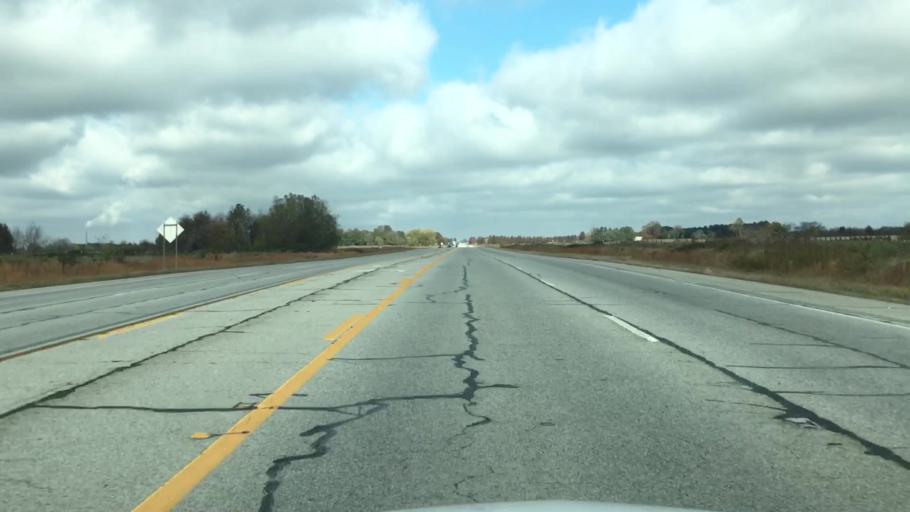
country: US
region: Arkansas
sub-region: Benton County
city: Siloam Springs
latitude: 36.1970
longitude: -94.4961
